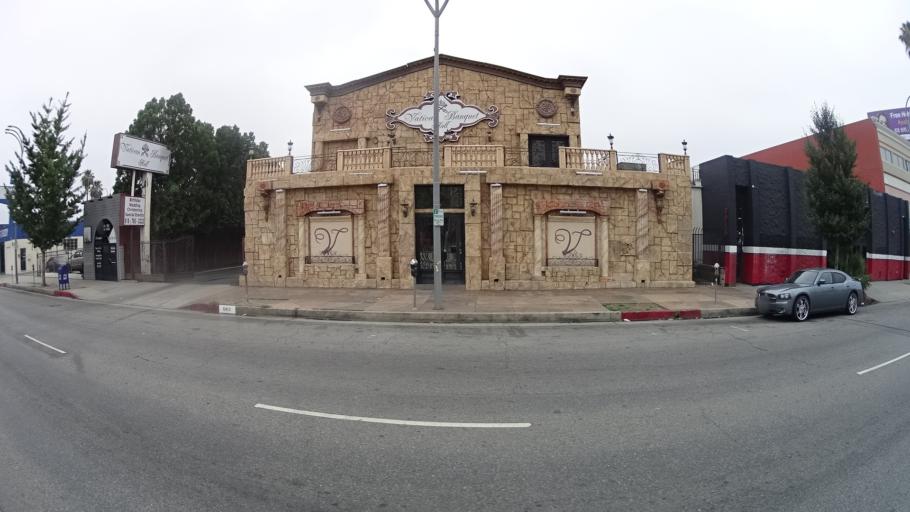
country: US
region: California
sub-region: Los Angeles County
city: Van Nuys
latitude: 34.1962
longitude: -118.4488
